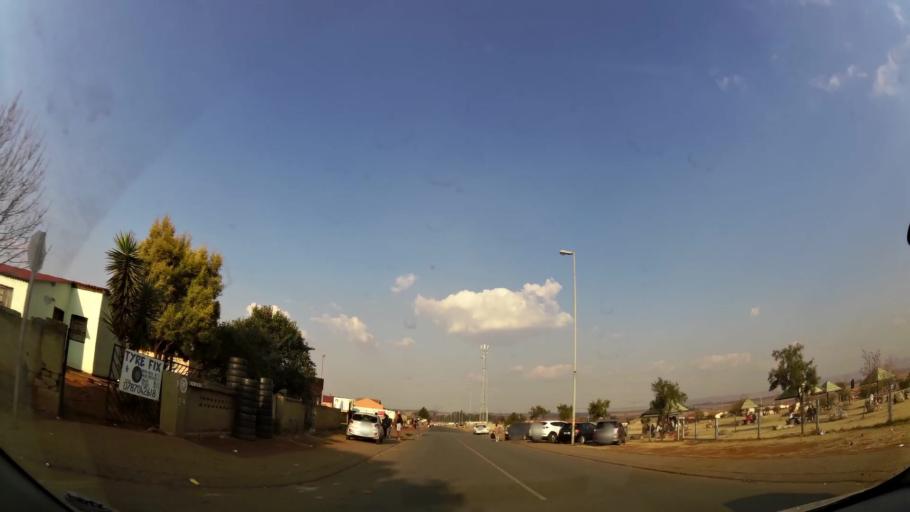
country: ZA
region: Gauteng
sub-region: Ekurhuleni Metropolitan Municipality
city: Germiston
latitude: -26.3617
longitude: 28.2251
